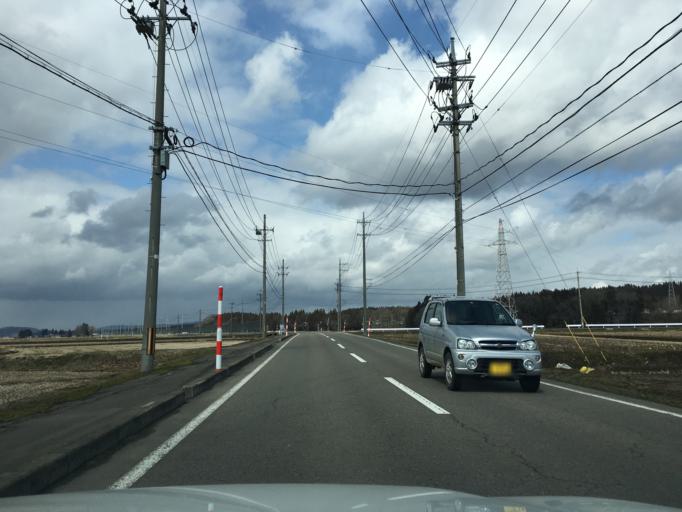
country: JP
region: Akita
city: Takanosu
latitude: 40.1255
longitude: 140.3655
